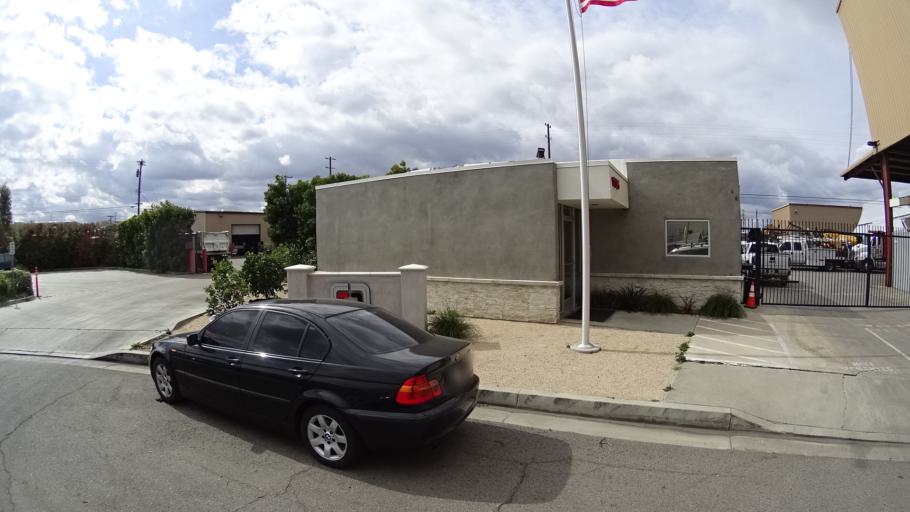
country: US
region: California
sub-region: Orange County
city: Placentia
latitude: 33.8511
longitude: -117.8671
